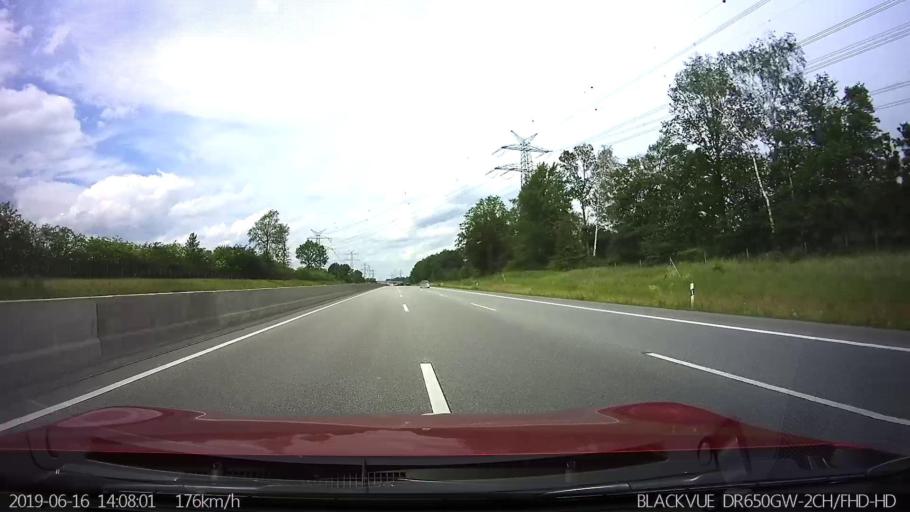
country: DE
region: Schleswig-Holstein
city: Alveslohe
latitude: 53.7759
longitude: 9.9437
